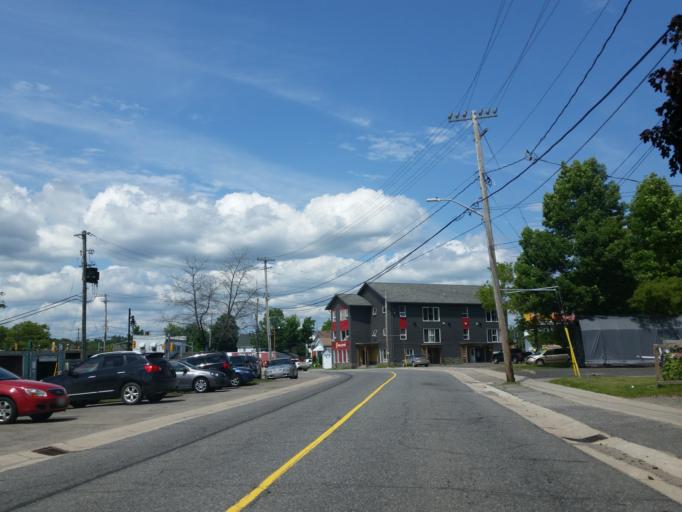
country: CA
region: Ontario
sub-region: Parry Sound District
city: Parry Sound
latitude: 45.3423
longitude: -80.0302
